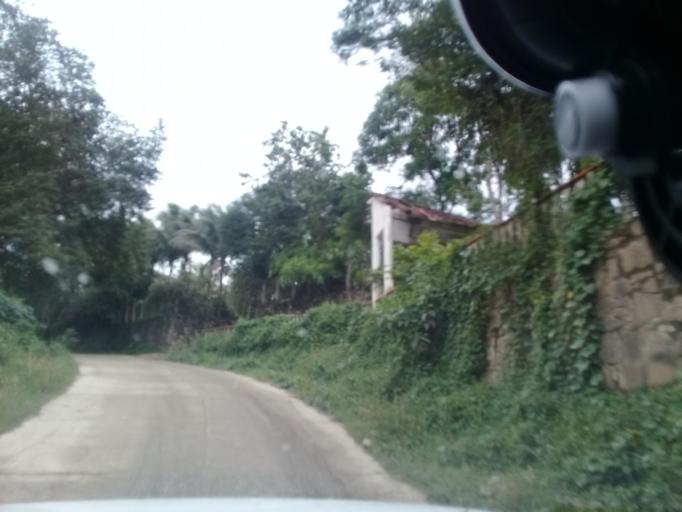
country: MX
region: Hidalgo
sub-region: Huejutla de Reyes
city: Chalahuiyapa
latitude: 21.1612
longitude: -98.3654
